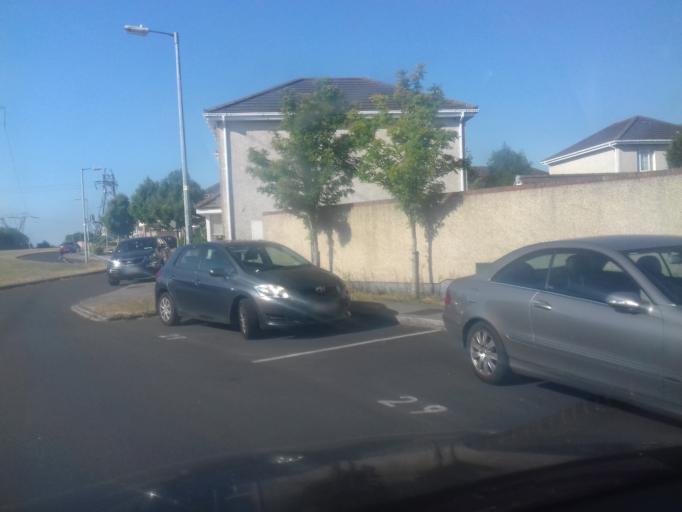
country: IE
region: Leinster
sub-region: Fingal County
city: Blanchardstown
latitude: 53.4210
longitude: -6.3956
